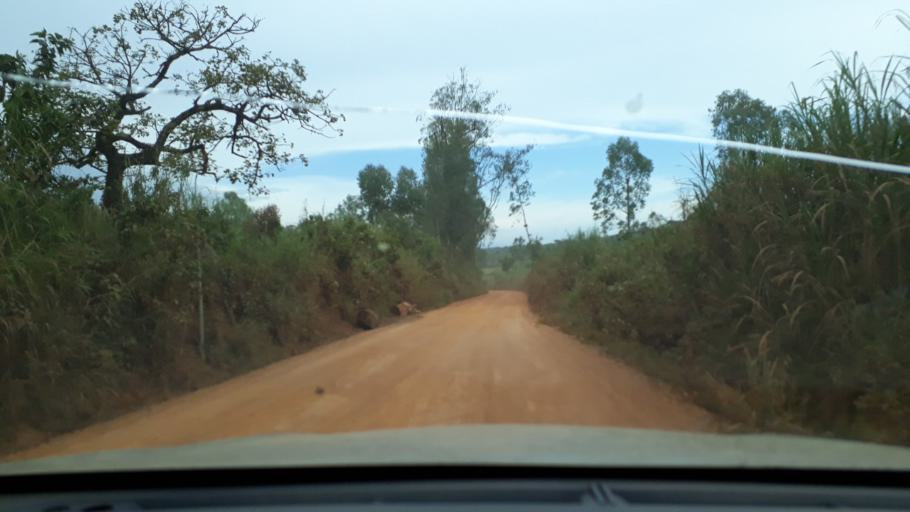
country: CD
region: Eastern Province
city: Bunia
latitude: 1.8663
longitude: 30.4791
